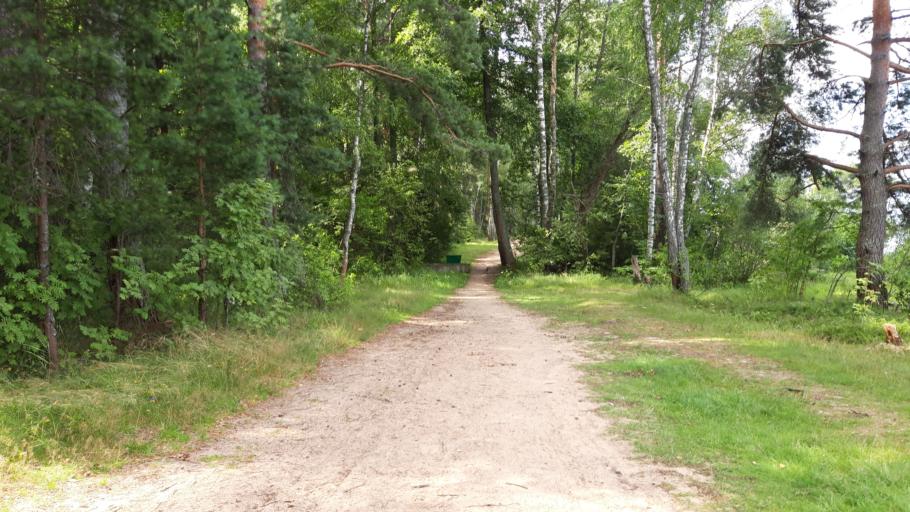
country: RU
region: Tverskaya
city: Konakovo
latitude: 56.6751
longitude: 36.6872
